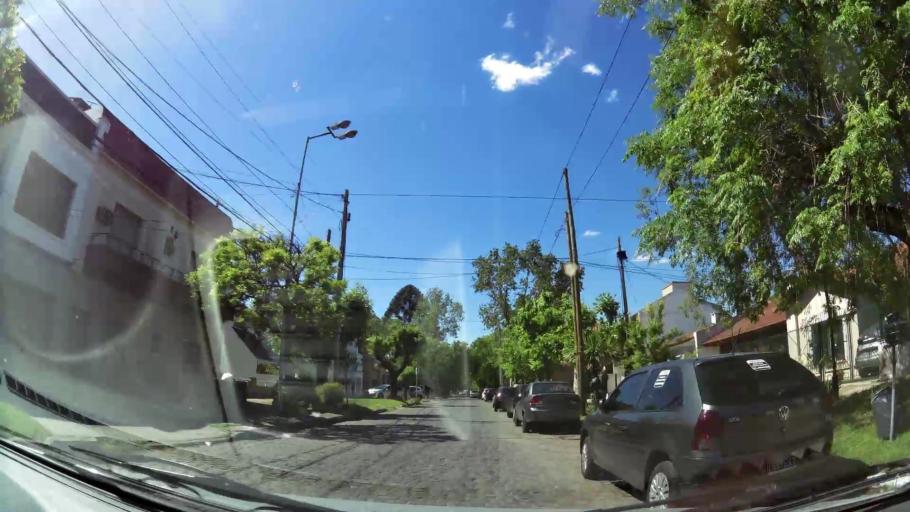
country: AR
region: Buenos Aires
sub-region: Partido de Lomas de Zamora
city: Lomas de Zamora
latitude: -34.7400
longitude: -58.4043
